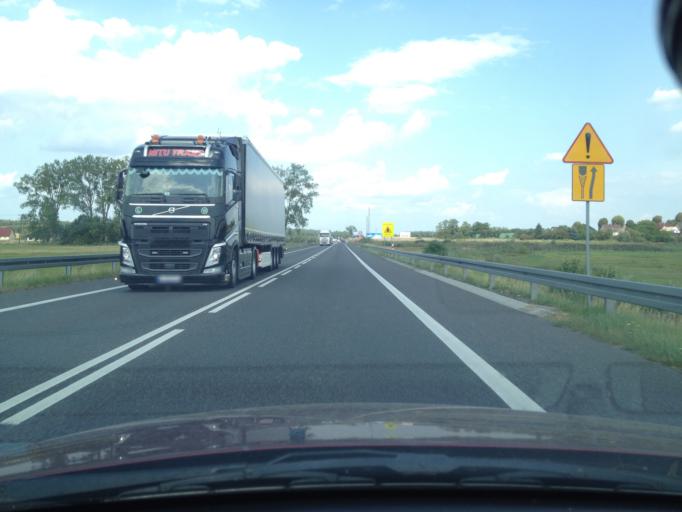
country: PL
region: West Pomeranian Voivodeship
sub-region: Powiat goleniowski
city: Przybiernow
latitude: 53.7544
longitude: 14.7751
